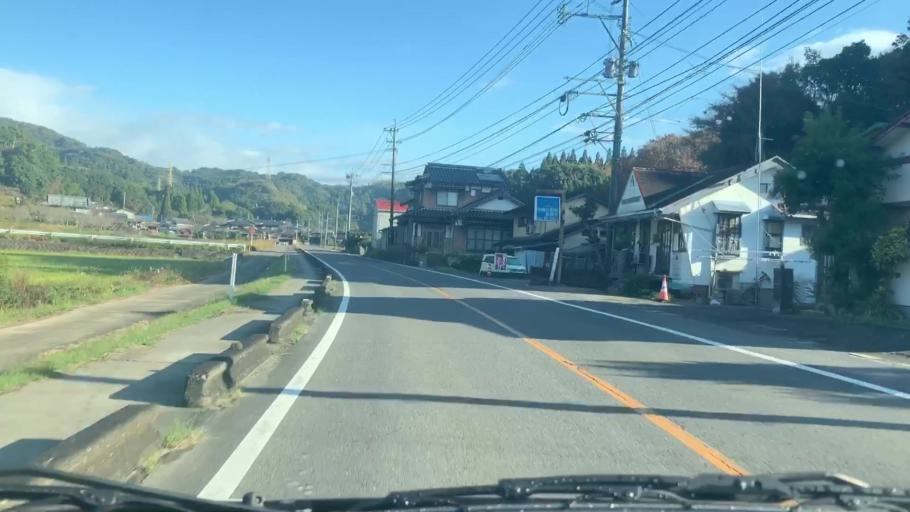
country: JP
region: Saga Prefecture
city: Takeocho-takeo
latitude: 33.2290
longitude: 130.0595
